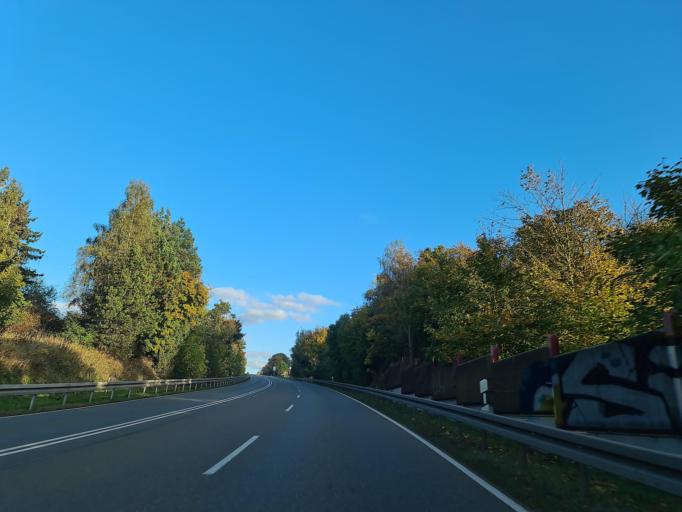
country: DE
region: Thuringia
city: Weida
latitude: 50.7724
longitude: 12.0699
